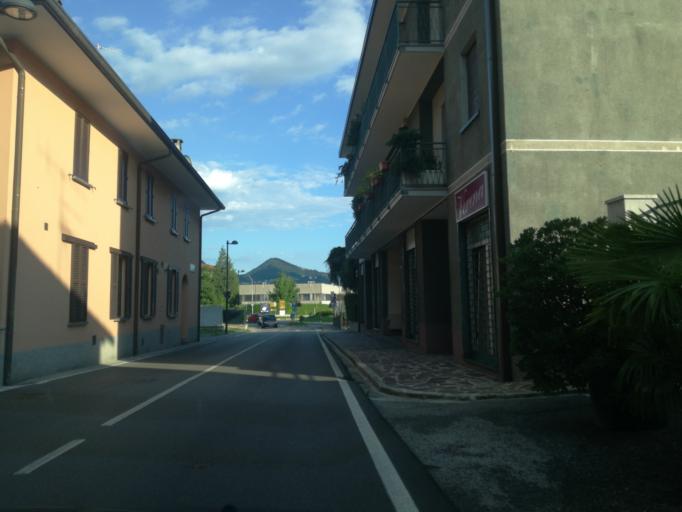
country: IT
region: Lombardy
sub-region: Provincia di Lecco
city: Vercurago
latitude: 45.8034
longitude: 9.4194
